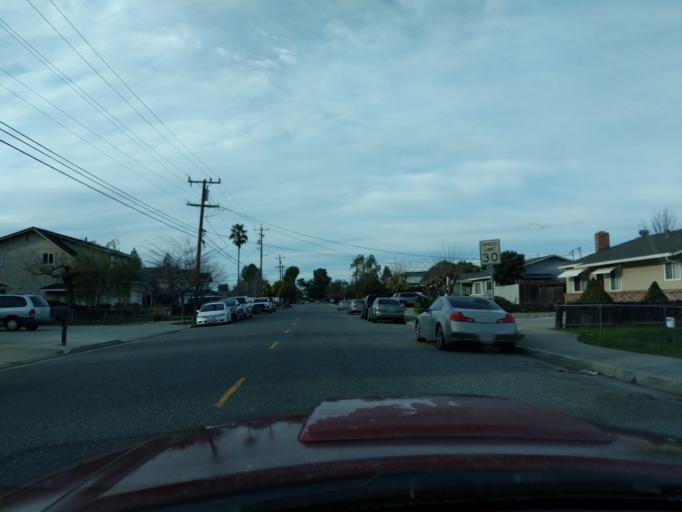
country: US
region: California
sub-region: Santa Clara County
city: Morgan Hill
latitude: 37.1161
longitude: -121.6422
